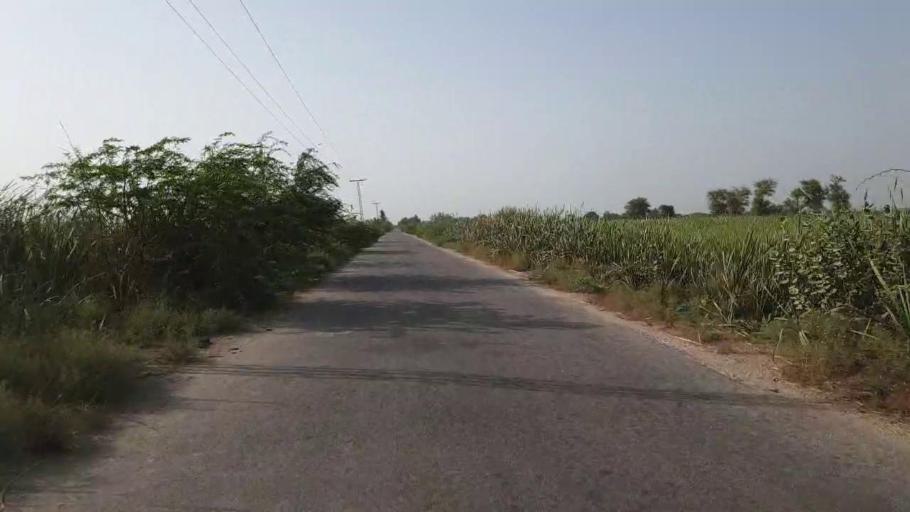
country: PK
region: Sindh
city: Jam Sahib
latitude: 26.4001
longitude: 68.8781
